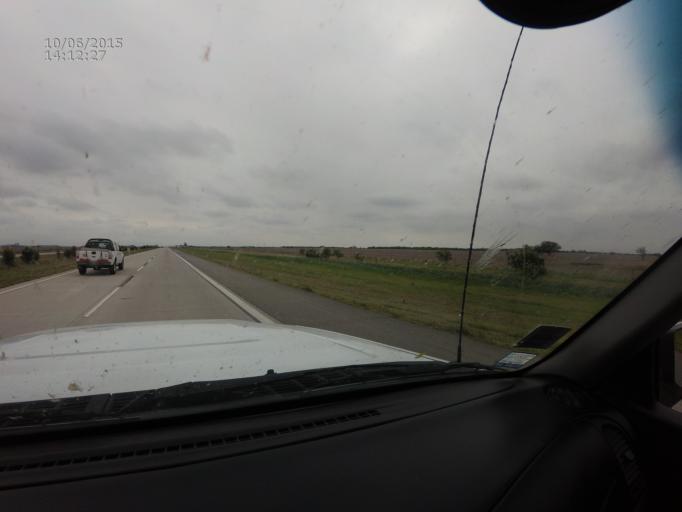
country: AR
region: Cordoba
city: Villa Maria
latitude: -32.4393
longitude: -63.1208
